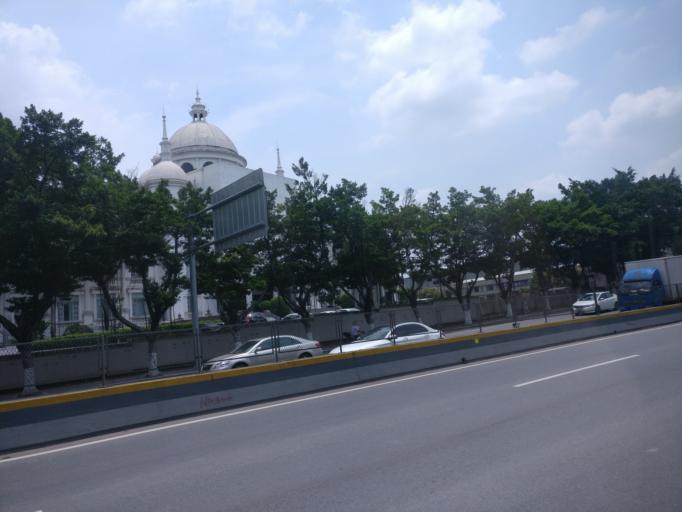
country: CN
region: Guangdong
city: Dashi
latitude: 23.0378
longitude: 113.3228
